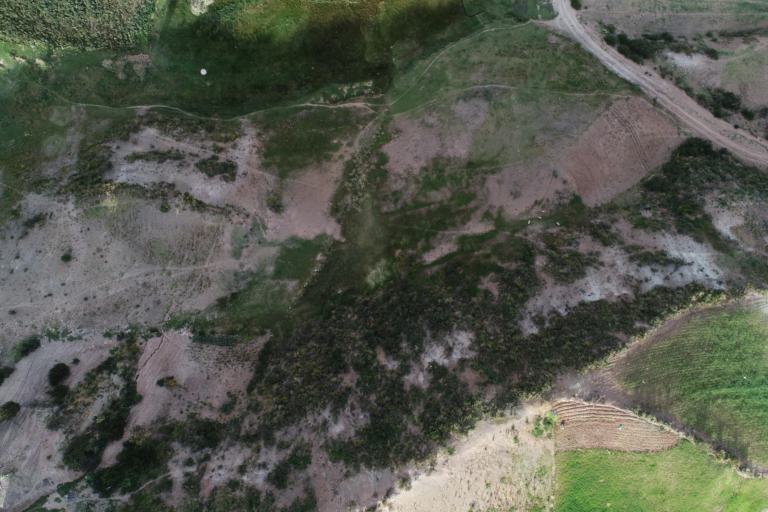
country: BO
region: La Paz
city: La Paz
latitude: -16.5441
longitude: -68.0028
